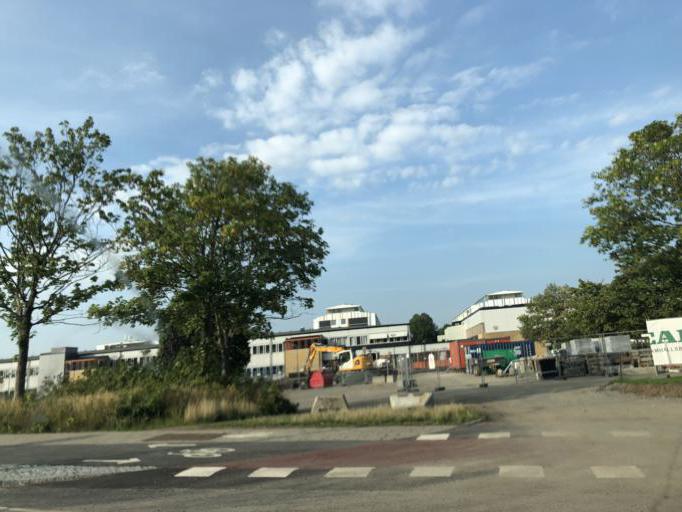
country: SE
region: Vaestra Goetaland
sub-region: Goteborg
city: Goeteborg
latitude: 57.7481
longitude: 11.9854
